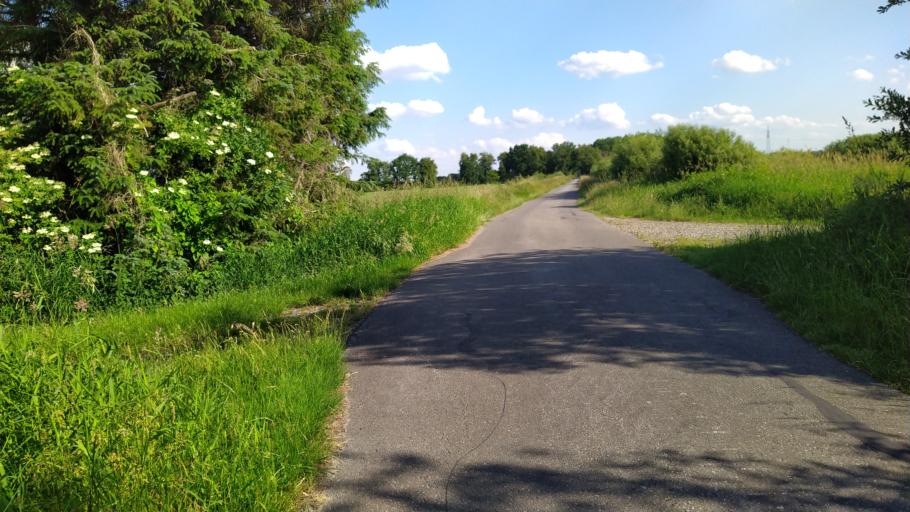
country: DE
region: Lower Saxony
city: Lintig
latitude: 53.6180
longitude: 8.8695
